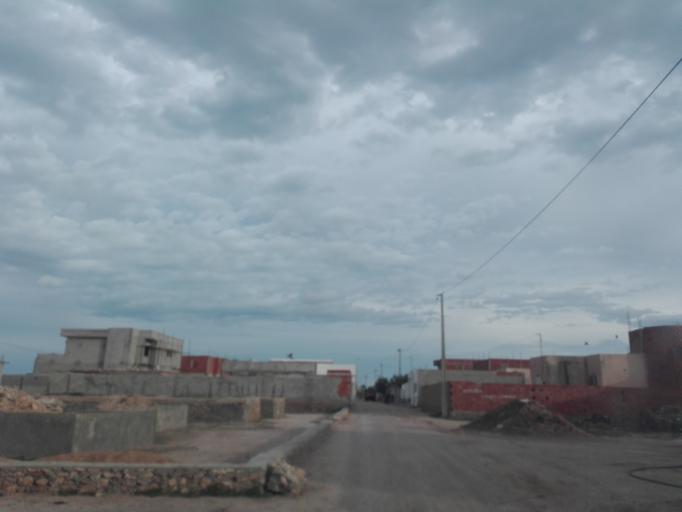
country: TN
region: Safaqis
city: Al Qarmadah
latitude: 34.8079
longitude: 10.8600
